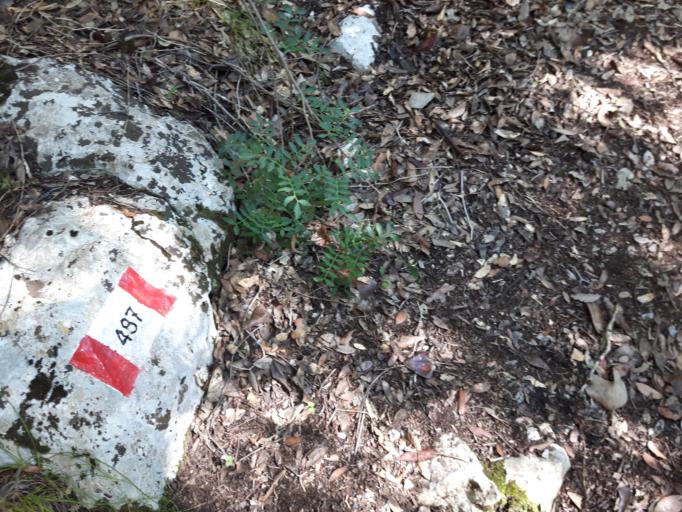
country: IT
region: Sardinia
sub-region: Provincia di Nuoro
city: Dorgali
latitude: 40.2305
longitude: 9.5117
